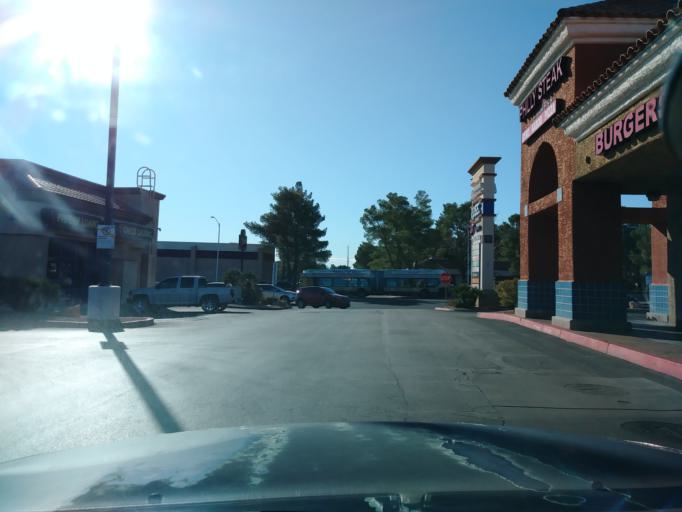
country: US
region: Nevada
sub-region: Clark County
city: Spring Valley
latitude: 36.1597
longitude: -115.2450
